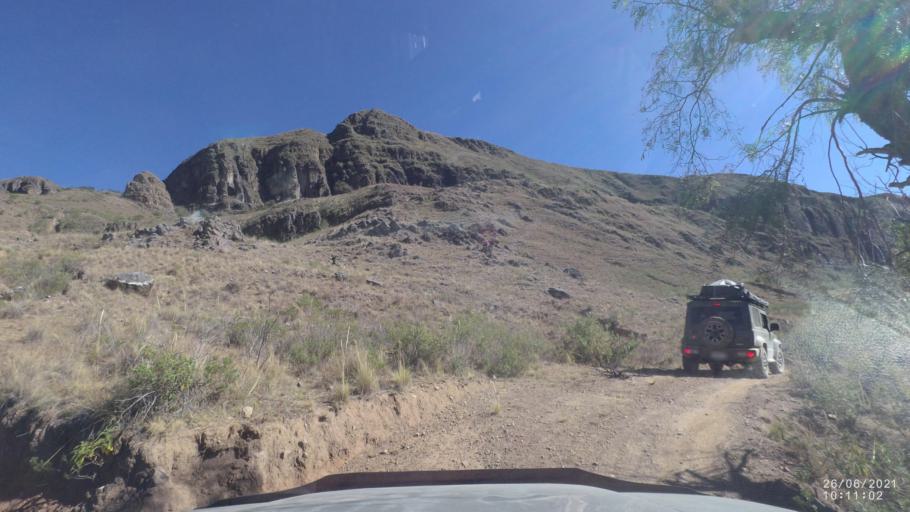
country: BO
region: Cochabamba
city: Mizque
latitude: -17.9171
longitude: -65.6259
